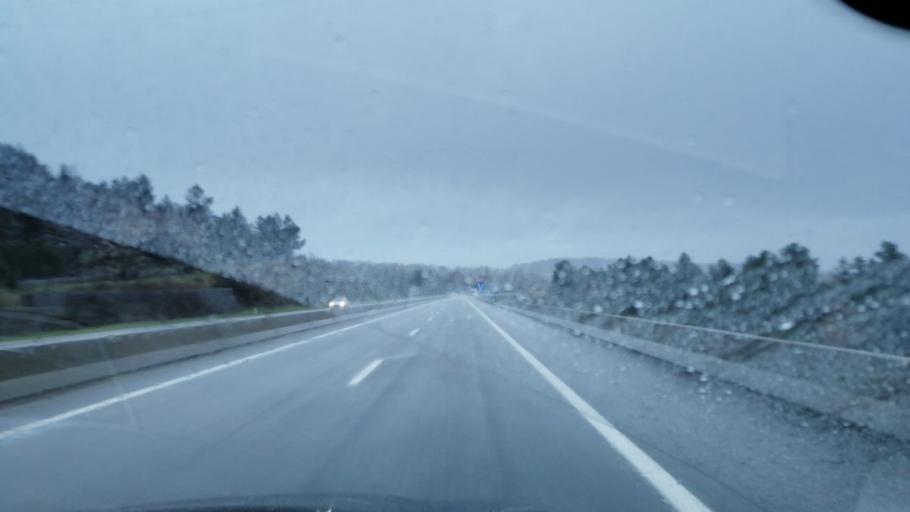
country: PT
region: Vila Real
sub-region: Sabrosa
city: Sabrosa
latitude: 41.3343
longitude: -7.6240
